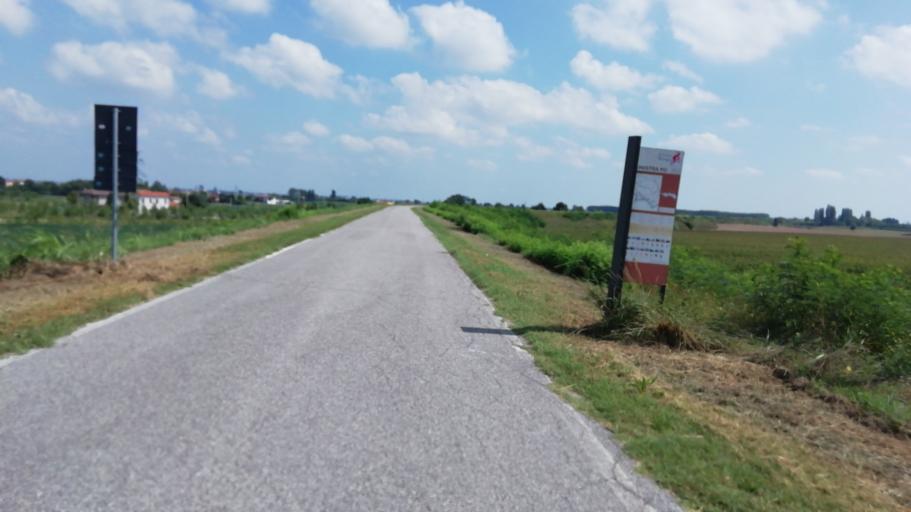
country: IT
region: Veneto
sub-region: Provincia di Rovigo
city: Gaiba
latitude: 44.9436
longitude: 11.4979
